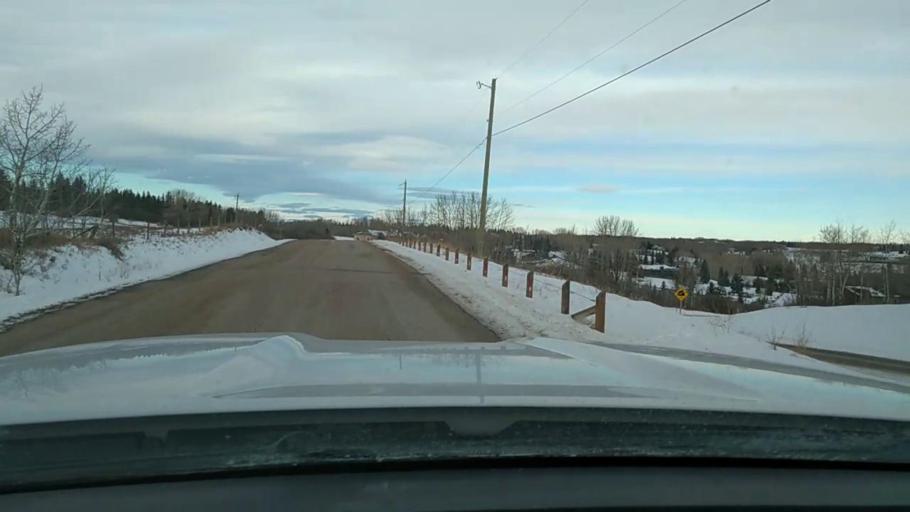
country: CA
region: Alberta
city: Cochrane
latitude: 51.1502
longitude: -114.2679
